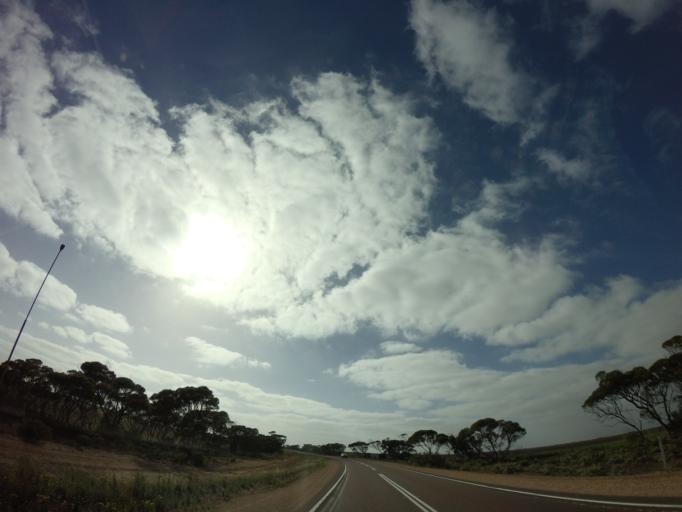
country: AU
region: South Australia
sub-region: Streaky Bay
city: Streaky Bay
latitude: -32.2797
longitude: 134.2194
